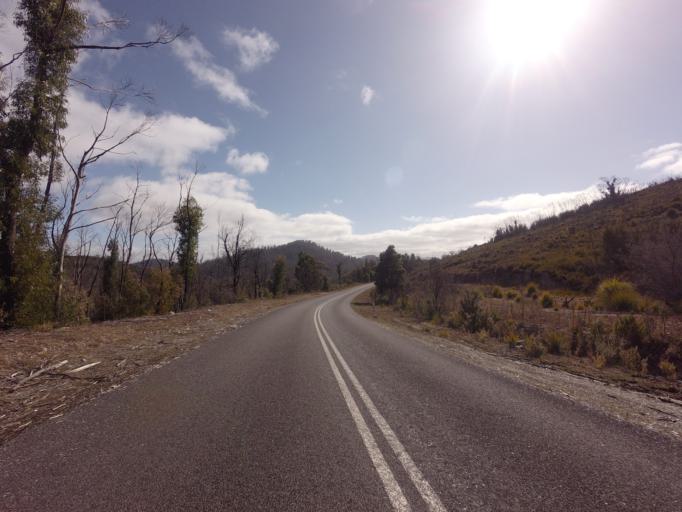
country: AU
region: Tasmania
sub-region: Huon Valley
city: Geeveston
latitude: -42.8508
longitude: 146.2352
